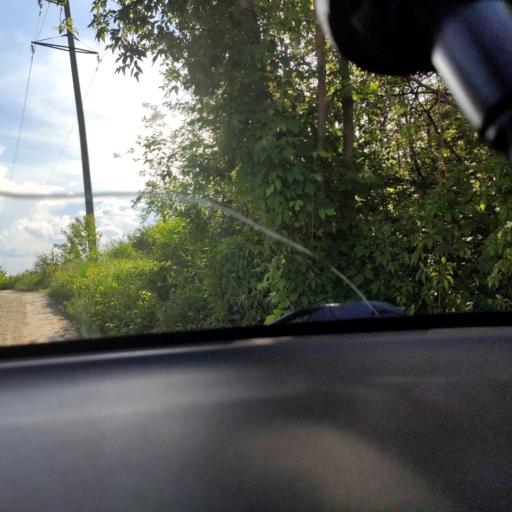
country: RU
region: Tatarstan
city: Verkhniy Uslon
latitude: 55.6479
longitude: 48.9436
